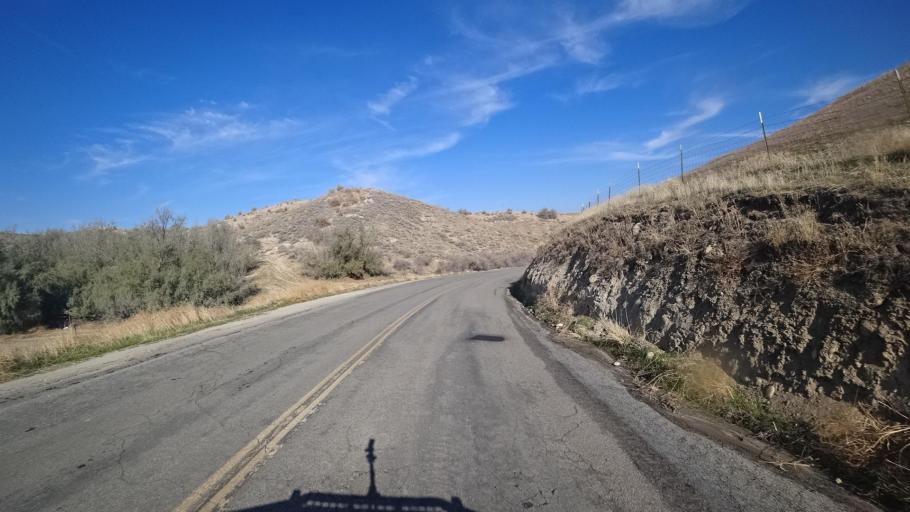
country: US
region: California
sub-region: Kern County
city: Lamont
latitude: 35.3932
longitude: -118.8182
